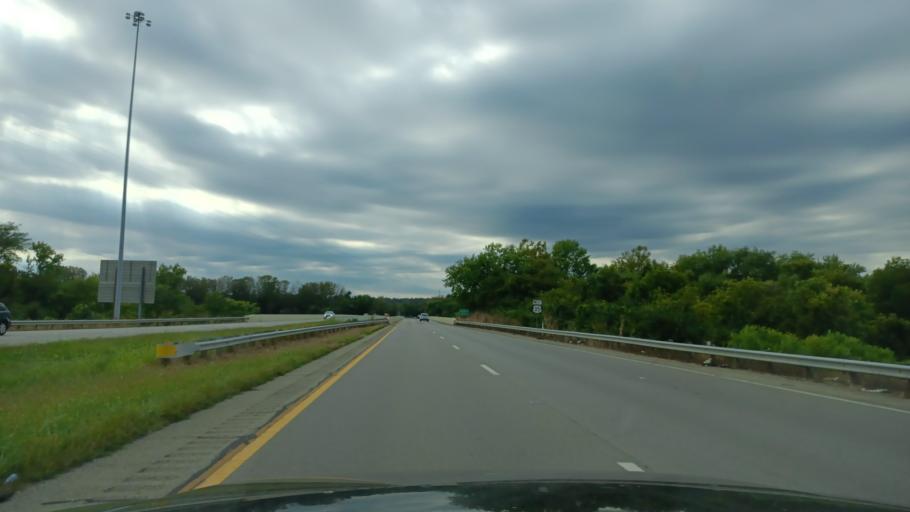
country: US
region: Ohio
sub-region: Ross County
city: Chillicothe
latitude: 39.3482
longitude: -82.9808
